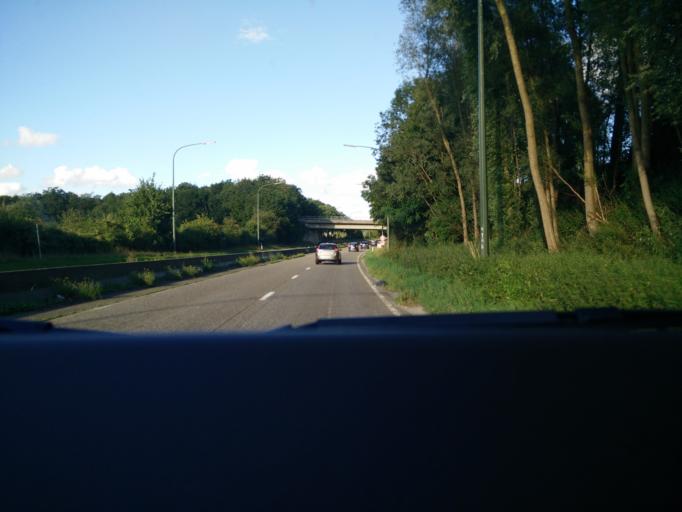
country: BE
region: Wallonia
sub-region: Province de Namur
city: Philippeville
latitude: 50.1998
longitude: 4.5406
